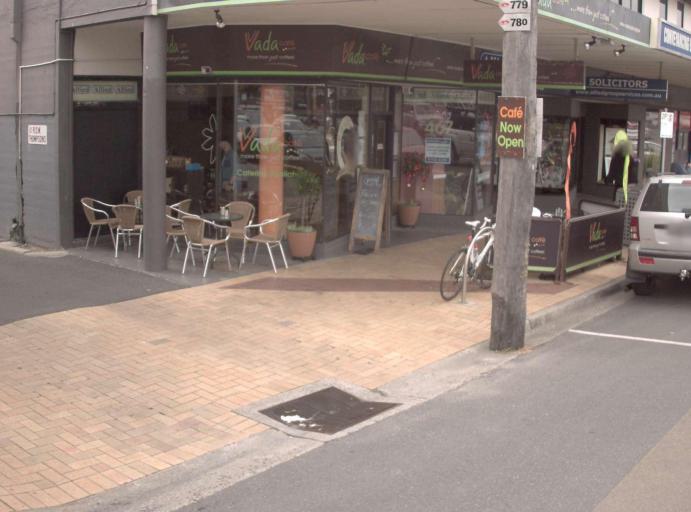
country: AU
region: Victoria
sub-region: Frankston
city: Frankston
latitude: -38.1439
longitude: 145.1209
